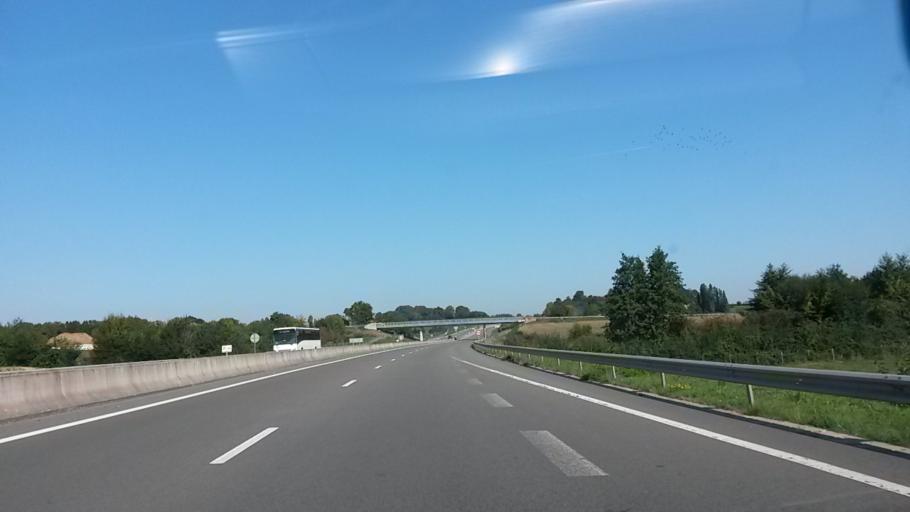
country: FR
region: Nord-Pas-de-Calais
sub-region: Departement du Nord
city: Hautmont
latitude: 50.2088
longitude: 3.9543
